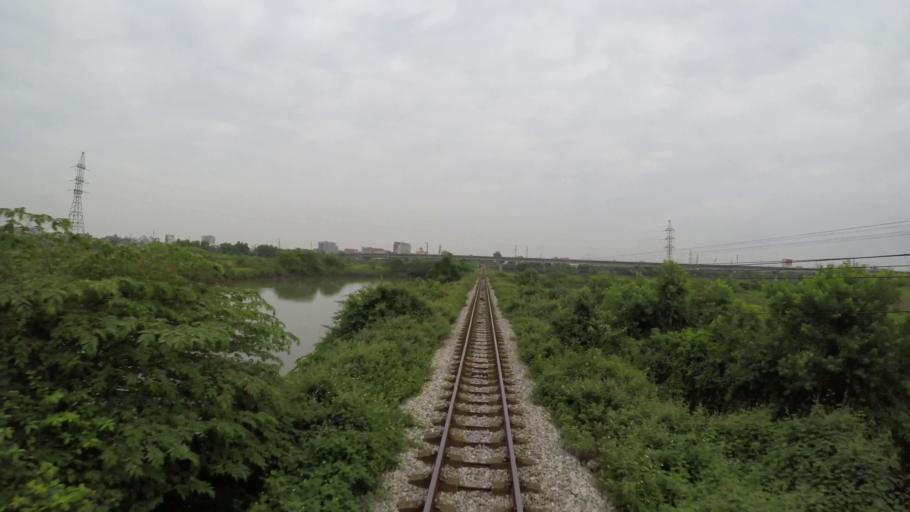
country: VN
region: Hai Phong
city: An Duong
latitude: 20.9102
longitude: 106.5705
